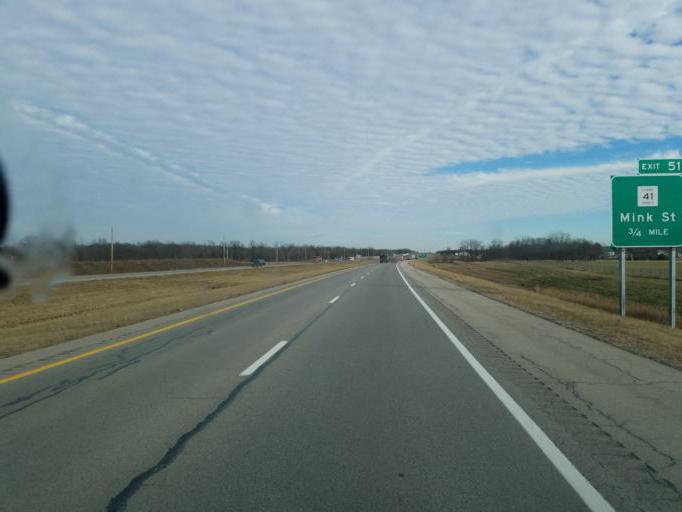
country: US
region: Ohio
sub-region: Franklin County
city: New Albany
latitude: 40.0808
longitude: -82.7424
